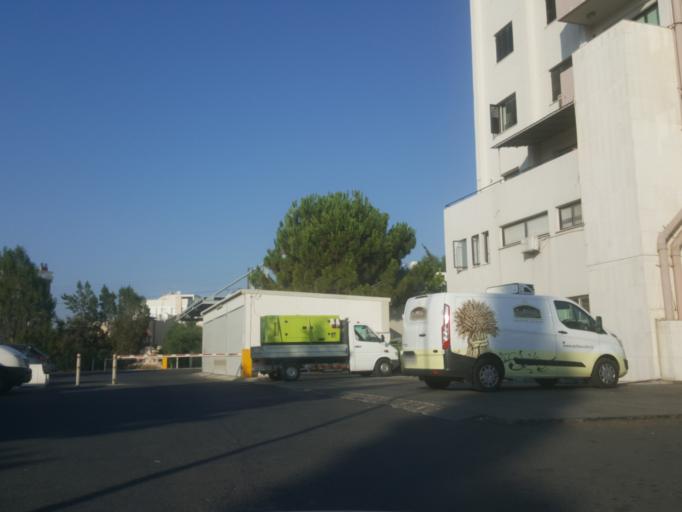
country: CY
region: Lefkosia
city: Nicosia
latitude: 35.1528
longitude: 33.3672
